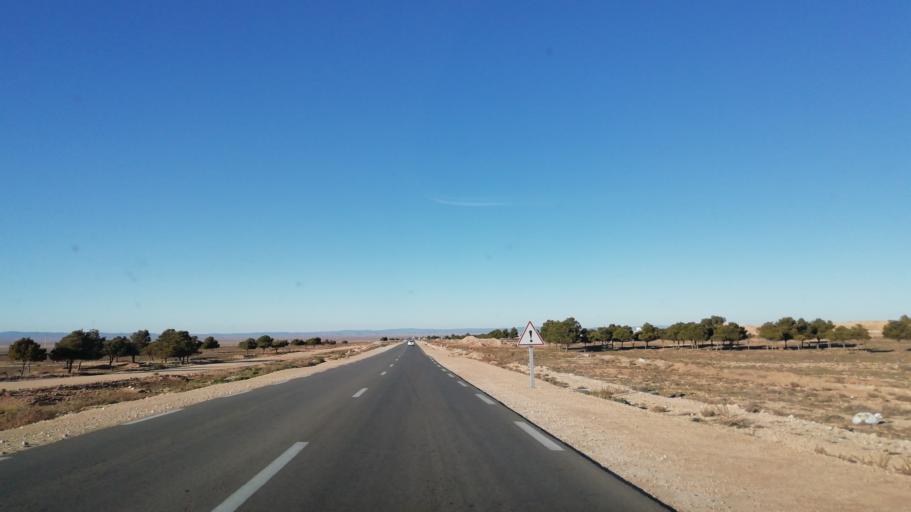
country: DZ
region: Tlemcen
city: Sebdou
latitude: 34.2925
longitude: -1.2602
